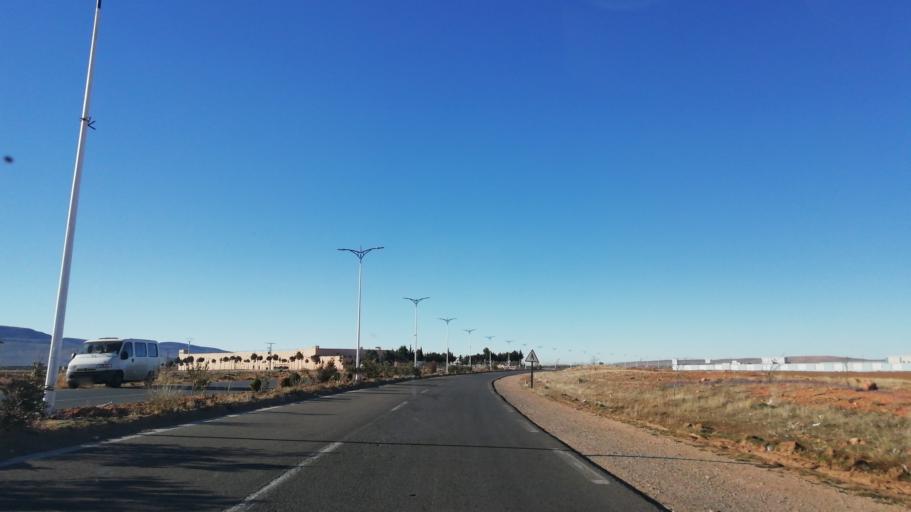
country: DZ
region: El Bayadh
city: El Bayadh
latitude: 33.6930
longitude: 1.0787
